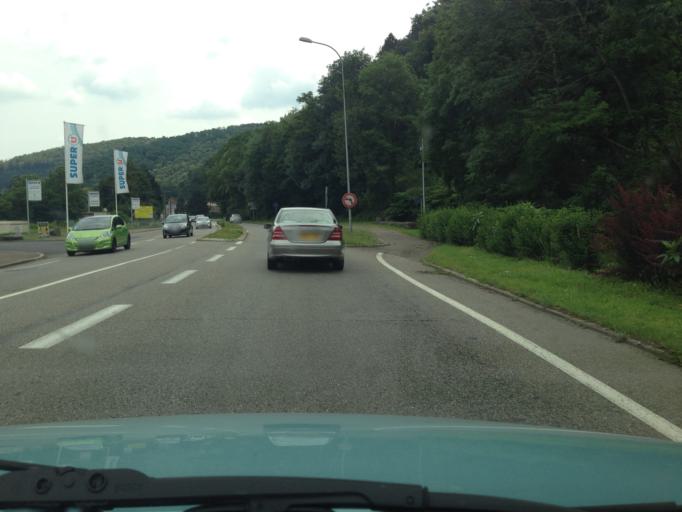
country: FR
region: Alsace
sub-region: Departement du Haut-Rhin
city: Thann
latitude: 47.8204
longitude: 7.0824
